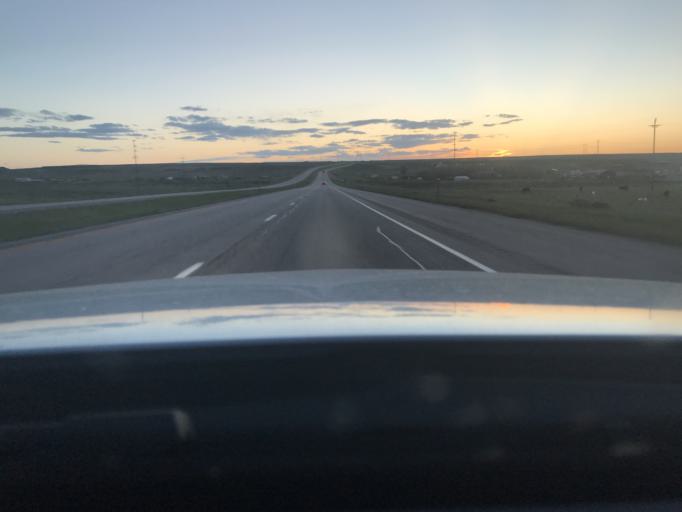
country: US
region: Wyoming
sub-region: Converse County
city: Glenrock
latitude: 42.8257
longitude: -105.8099
